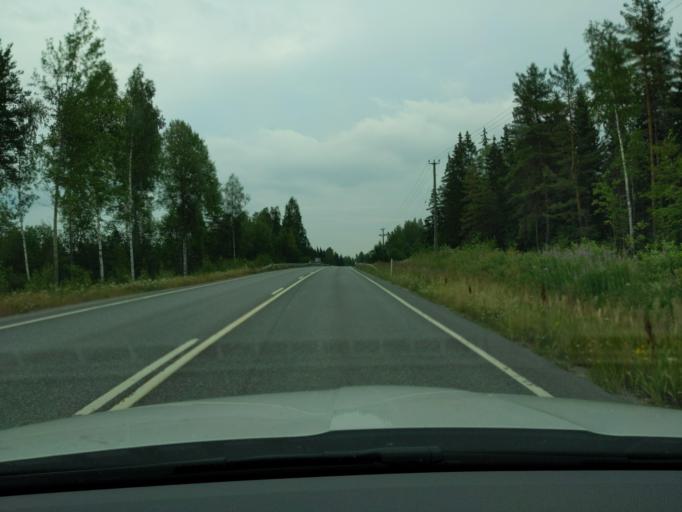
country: FI
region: Uusimaa
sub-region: Helsinki
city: Nickby
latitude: 60.3561
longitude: 25.3980
